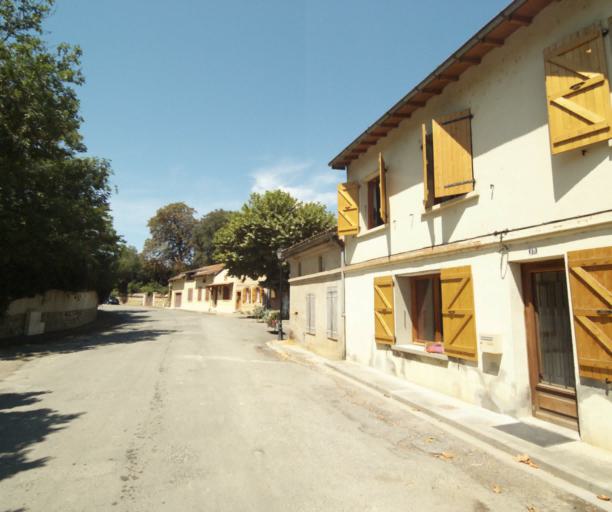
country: FR
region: Midi-Pyrenees
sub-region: Departement de l'Ariege
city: Lezat-sur-Leze
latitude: 43.2747
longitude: 1.3518
